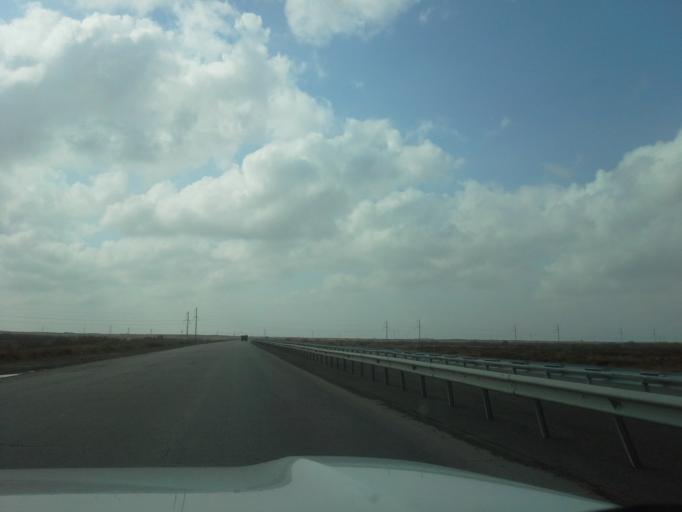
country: TM
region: Mary
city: Mary
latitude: 37.3441
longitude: 61.4288
